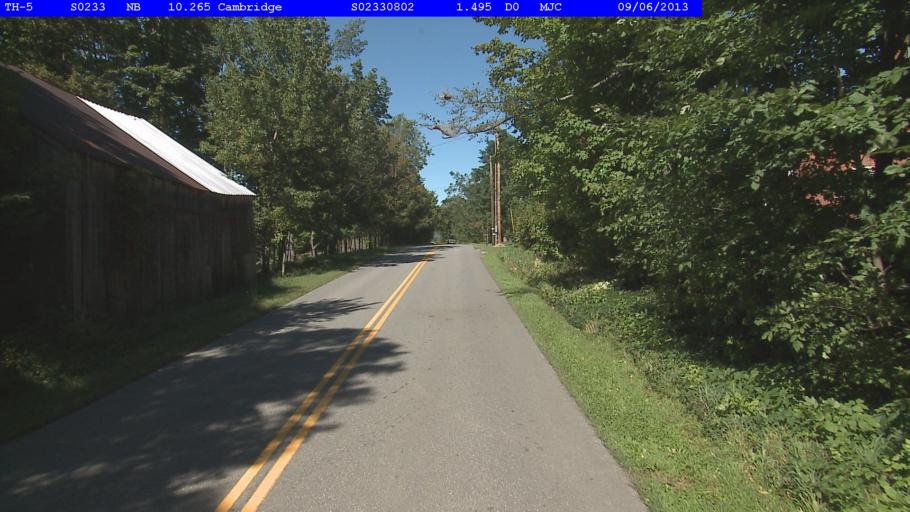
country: US
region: Vermont
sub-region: Chittenden County
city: Jericho
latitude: 44.6033
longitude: -72.8568
